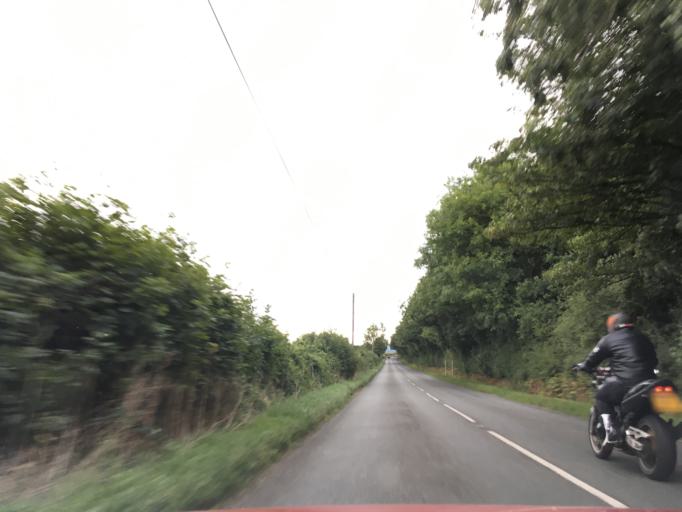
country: GB
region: England
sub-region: Wiltshire
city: Bremhill
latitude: 51.4194
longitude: -2.0605
